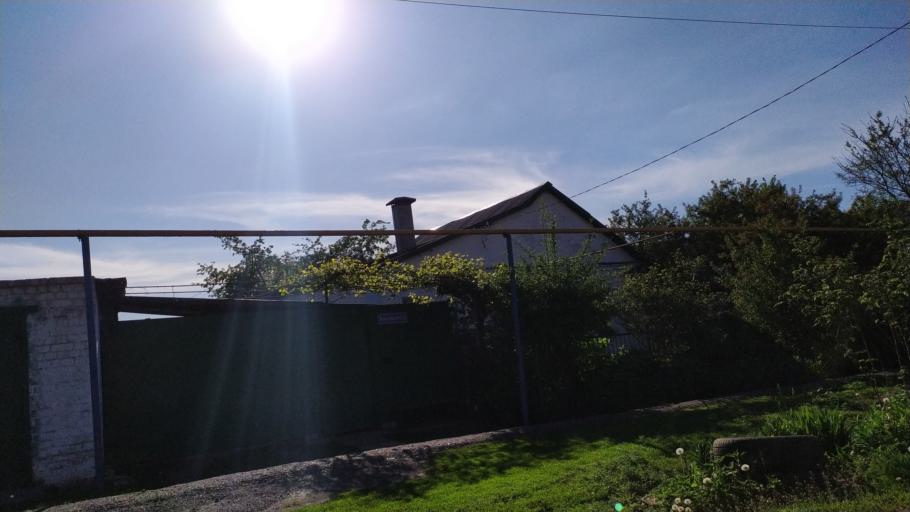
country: RU
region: Kursk
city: Kursk
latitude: 51.6398
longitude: 36.1480
